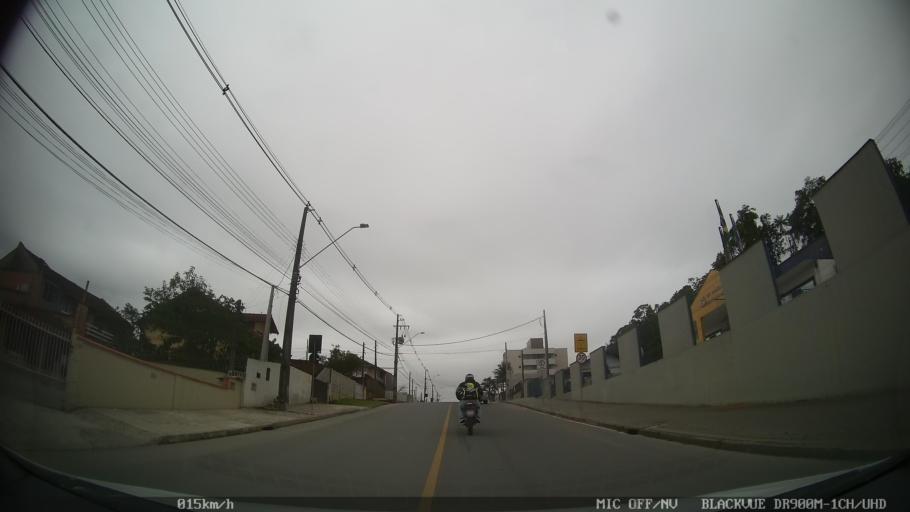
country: BR
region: Santa Catarina
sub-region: Joinville
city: Joinville
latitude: -26.2773
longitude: -48.9033
